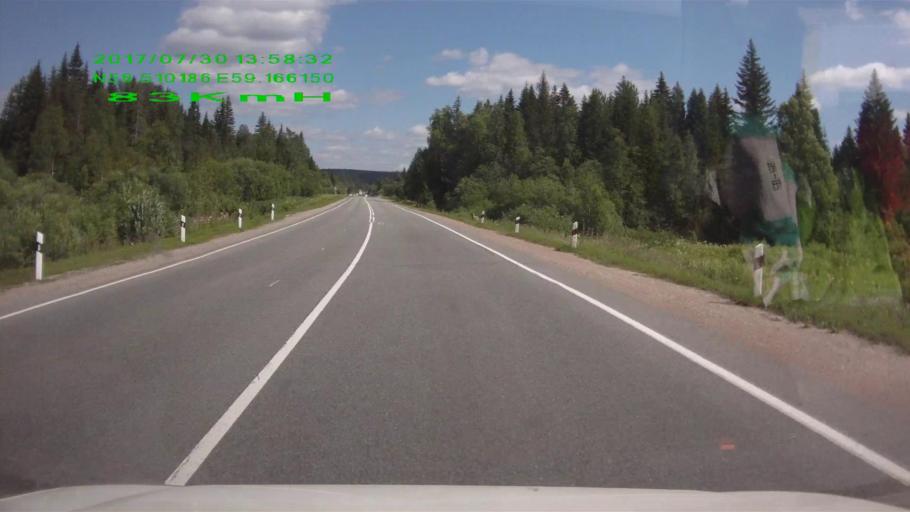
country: RU
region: Sverdlovsk
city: Mikhaylovsk
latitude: 56.5102
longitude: 59.1668
